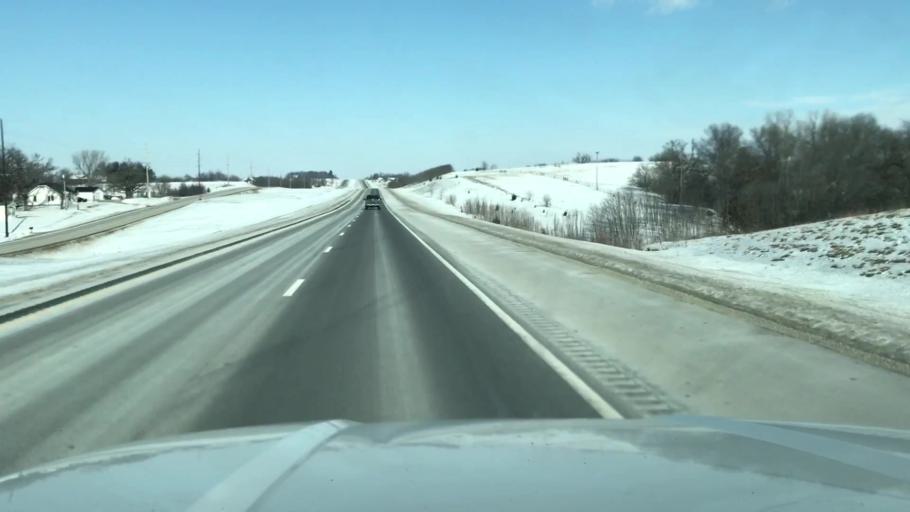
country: US
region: Missouri
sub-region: Nodaway County
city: Maryville
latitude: 40.1880
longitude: -94.8678
